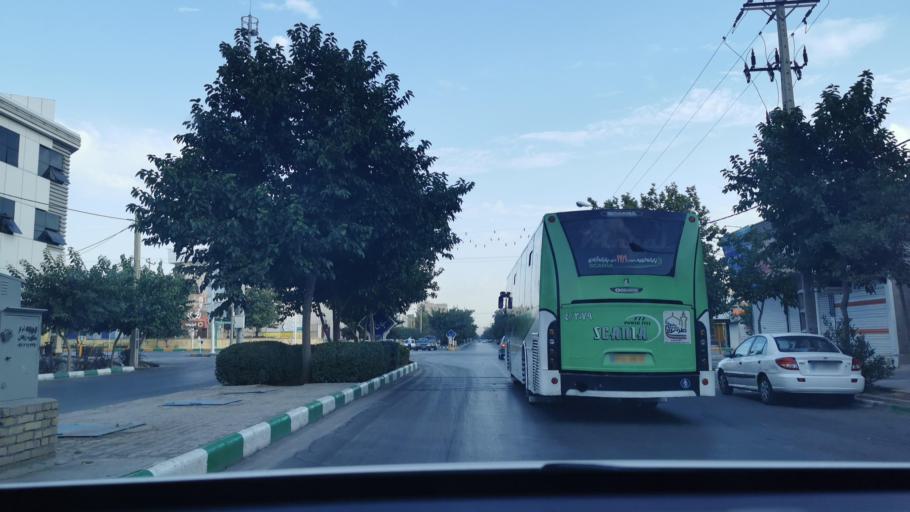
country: IR
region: Razavi Khorasan
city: Mashhad
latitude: 36.3559
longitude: 59.5264
